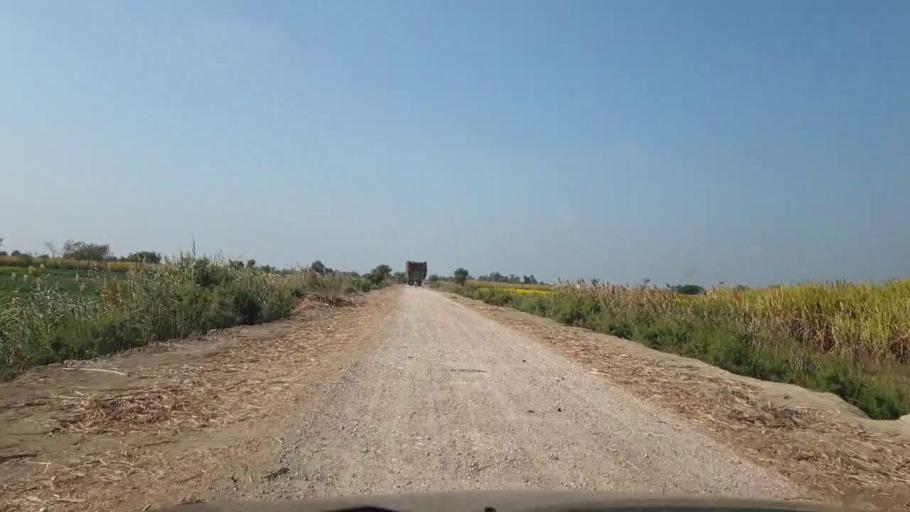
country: PK
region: Sindh
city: Sinjhoro
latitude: 26.0479
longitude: 68.7339
